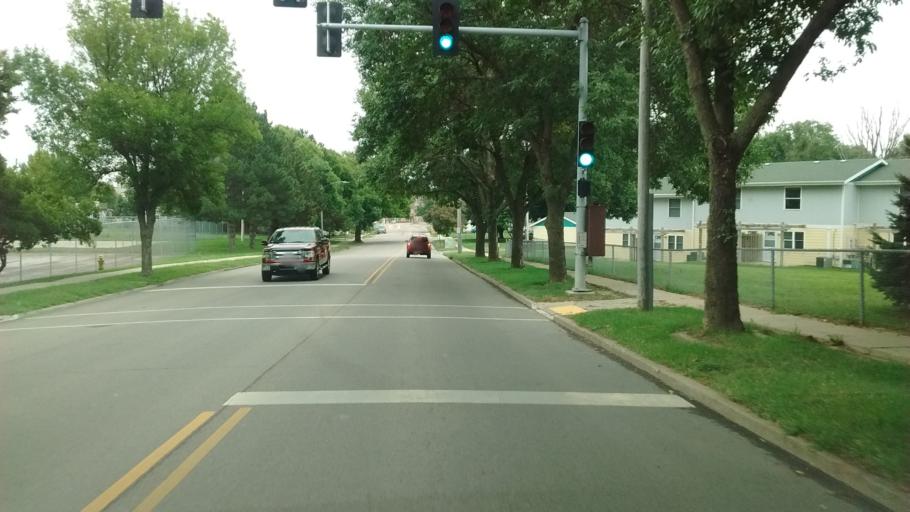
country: US
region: Iowa
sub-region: Woodbury County
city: Sioux City
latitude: 42.4982
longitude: -96.4161
